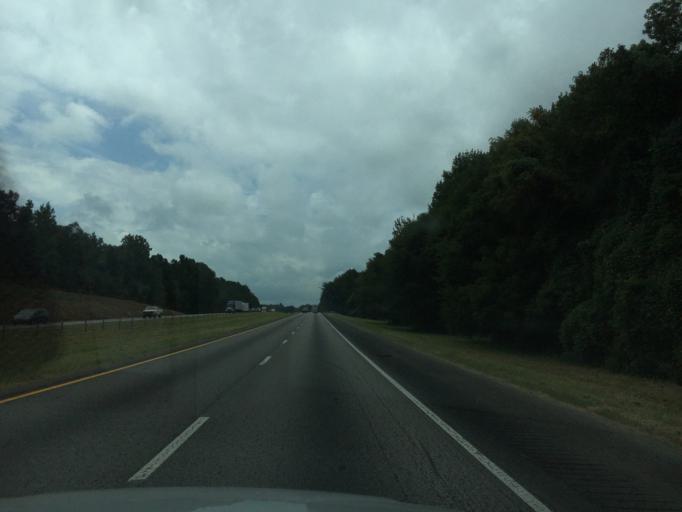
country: US
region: Georgia
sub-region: Jackson County
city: Jefferson
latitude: 34.1762
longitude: -83.6097
